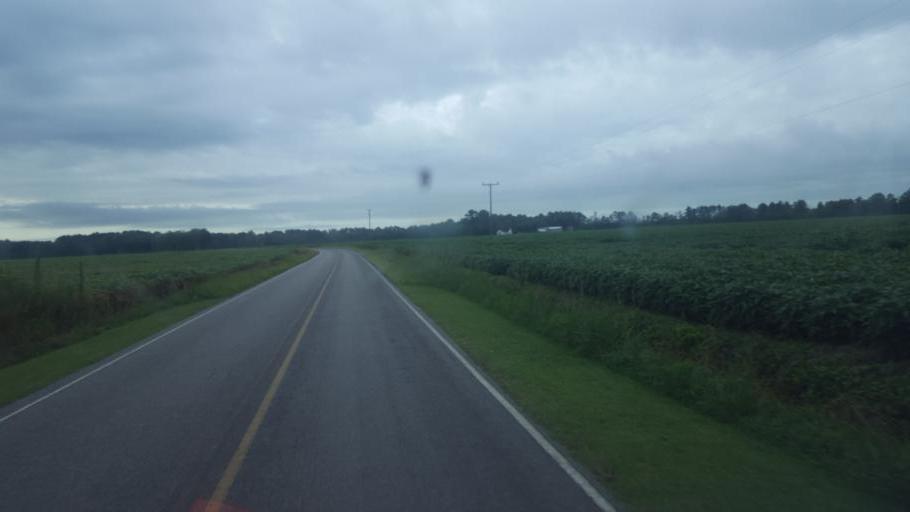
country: US
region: North Carolina
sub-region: Tyrrell County
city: Columbia
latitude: 35.9412
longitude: -76.2811
